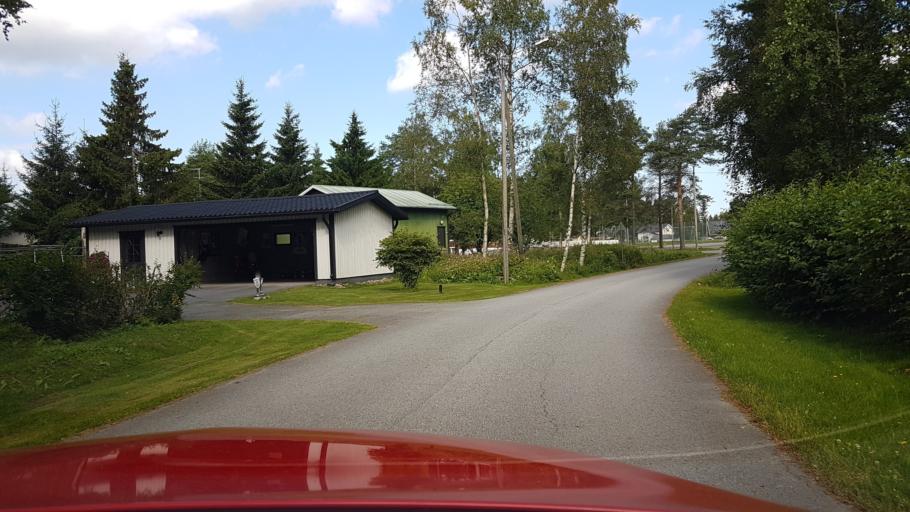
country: FI
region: Northern Ostrobothnia
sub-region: Ylivieska
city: Himanka
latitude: 64.0631
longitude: 23.6618
